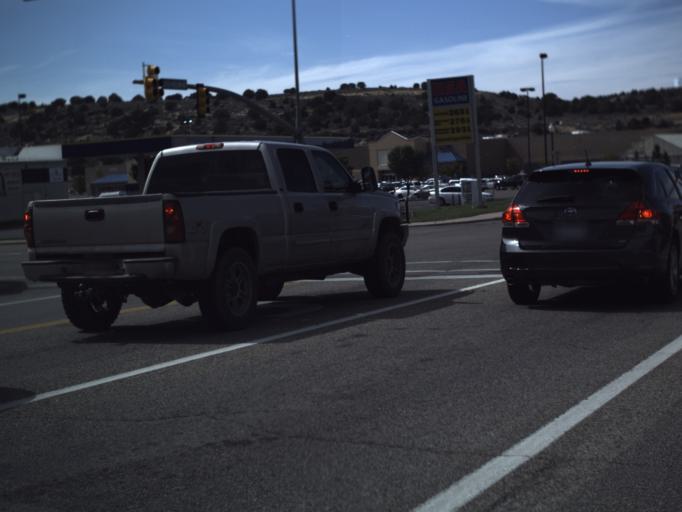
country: US
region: Utah
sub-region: Iron County
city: Cedar City
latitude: 37.6551
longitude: -113.0847
